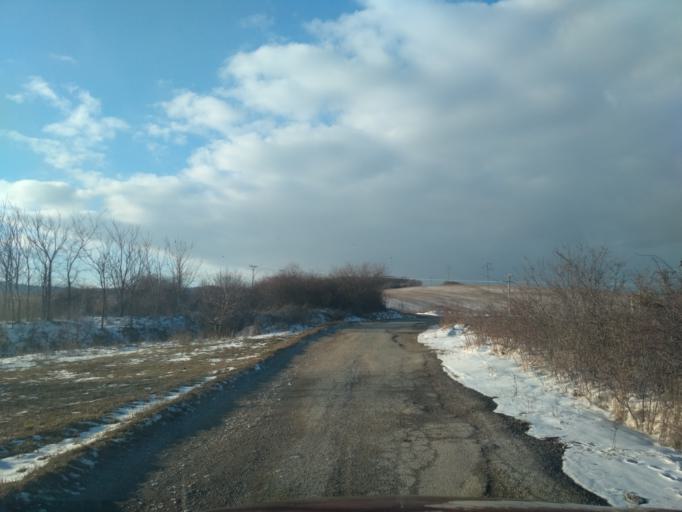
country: SK
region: Kosicky
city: Kosice
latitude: 48.7329
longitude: 21.1467
